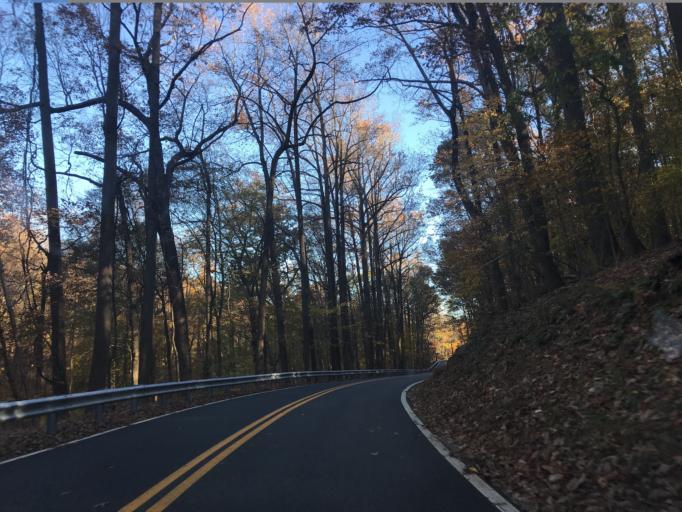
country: US
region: Maryland
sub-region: Baltimore County
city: Hampton
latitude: 39.4378
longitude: -76.5512
